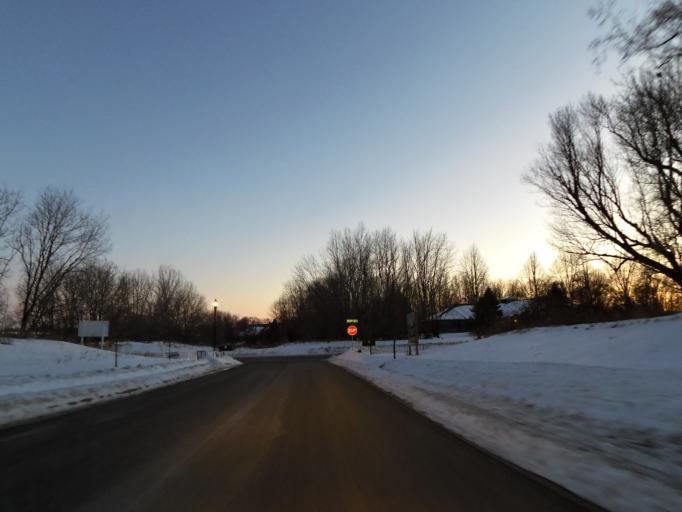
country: US
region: Minnesota
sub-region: Washington County
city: Lake Elmo
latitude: 45.0060
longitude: -92.8781
